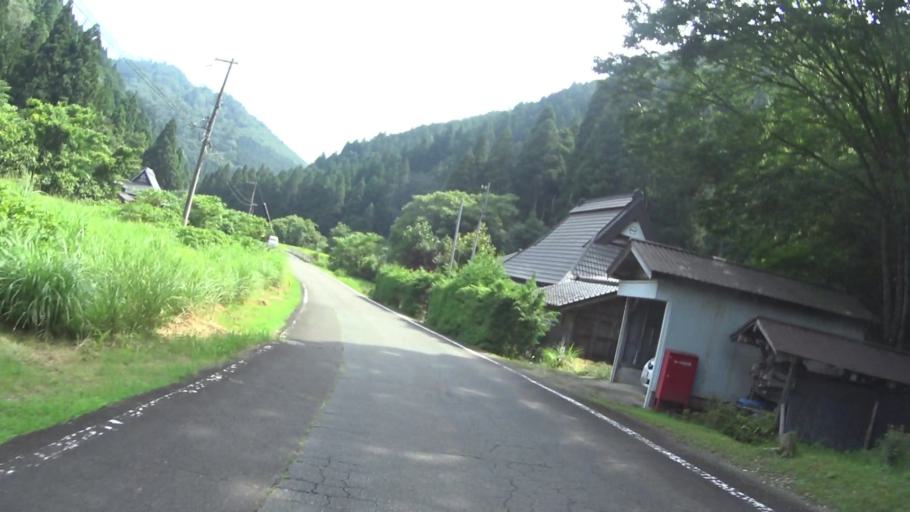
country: JP
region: Fukui
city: Obama
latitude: 35.3323
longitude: 135.6454
